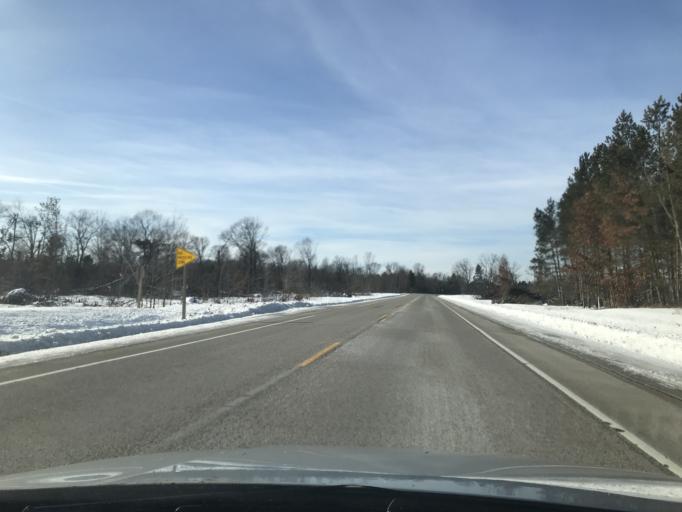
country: US
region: Wisconsin
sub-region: Oconto County
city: Gillett
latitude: 45.1147
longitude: -88.3713
